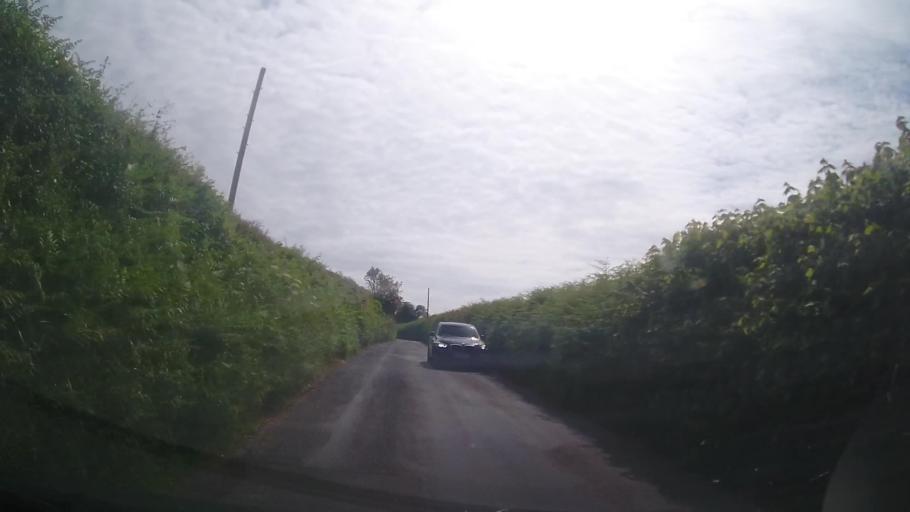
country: GB
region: England
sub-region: Devon
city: Salcombe
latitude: 50.2554
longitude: -3.6795
